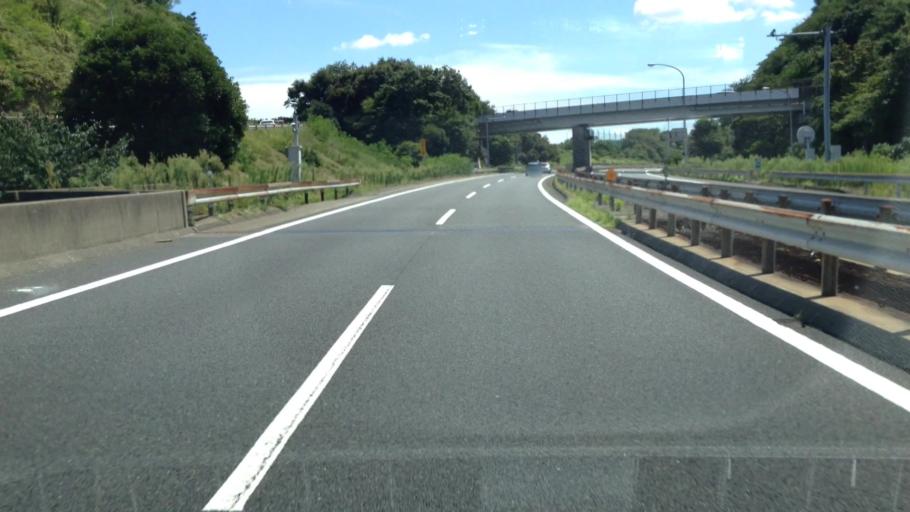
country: JP
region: Kanagawa
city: Yokosuka
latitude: 35.2782
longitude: 139.6332
